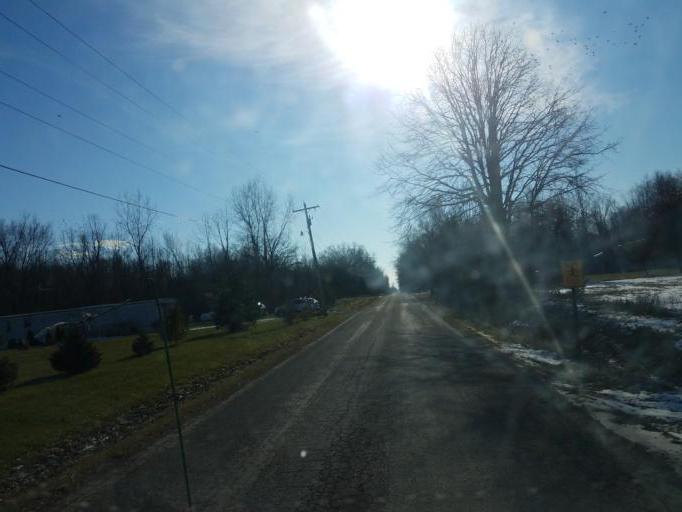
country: US
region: Ohio
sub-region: Morrow County
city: Cardington
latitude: 40.4904
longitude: -82.8682
